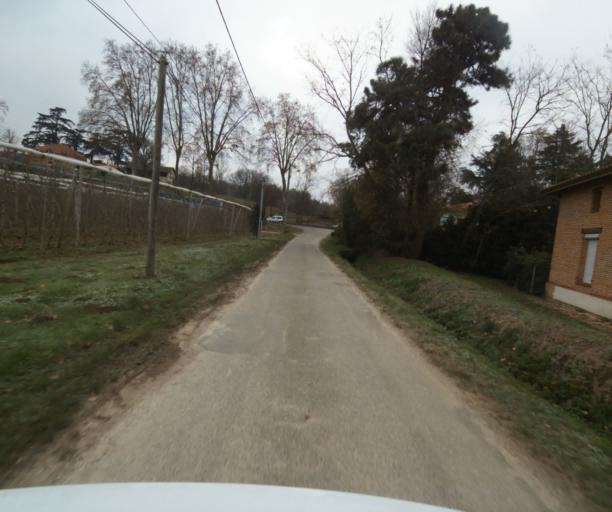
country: FR
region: Midi-Pyrenees
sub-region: Departement du Tarn-et-Garonne
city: Moissac
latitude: 44.1213
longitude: 1.1459
